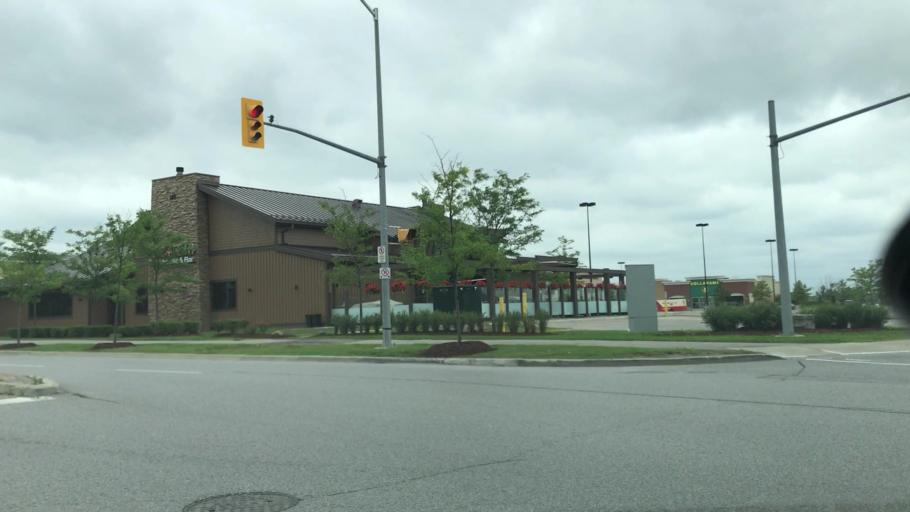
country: CA
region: Ontario
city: Newmarket
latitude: 44.0143
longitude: -79.4154
